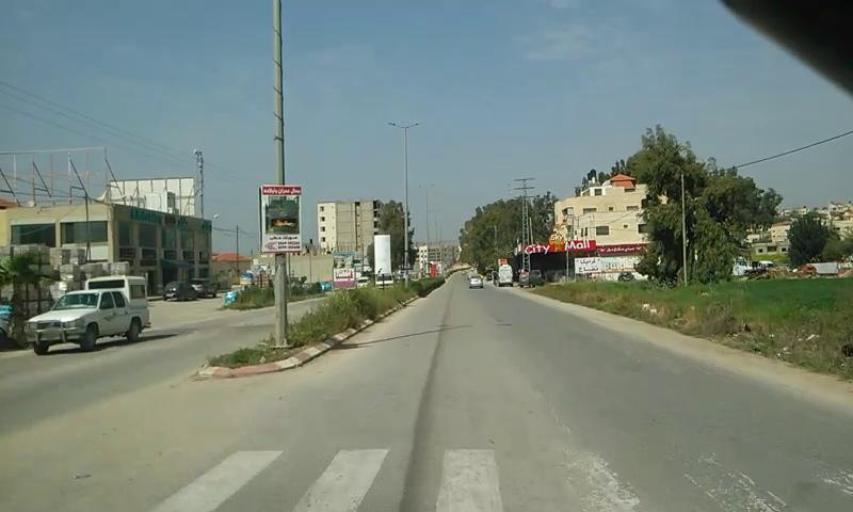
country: PS
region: West Bank
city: Janin
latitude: 32.4776
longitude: 35.3004
